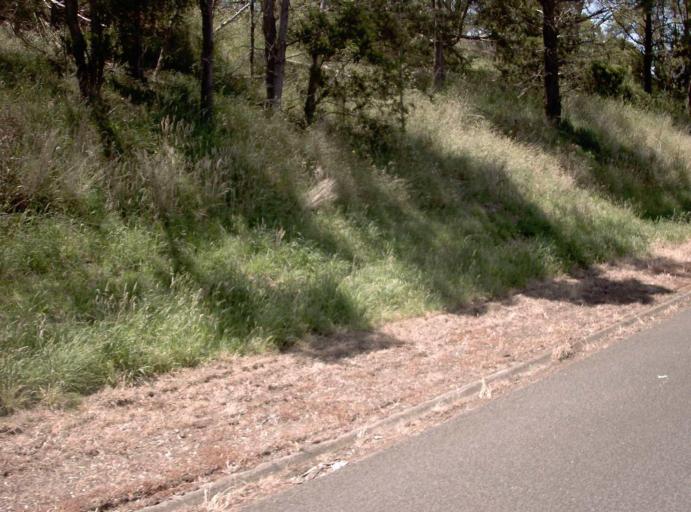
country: AU
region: Victoria
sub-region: Baw Baw
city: Warragul
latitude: -38.1562
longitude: 145.9028
